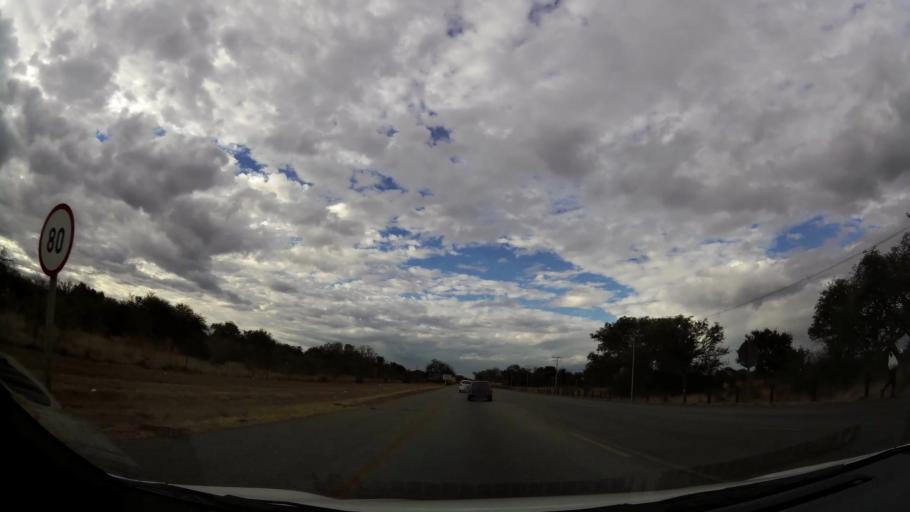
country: ZA
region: Limpopo
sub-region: Waterberg District Municipality
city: Modimolle
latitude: -24.5292
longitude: 28.7048
